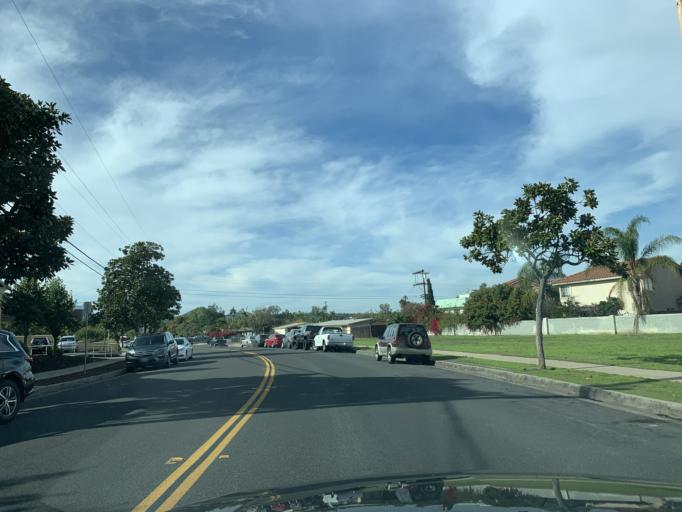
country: US
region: California
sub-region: San Diego County
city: El Cajon
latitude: 32.8004
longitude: -116.9521
